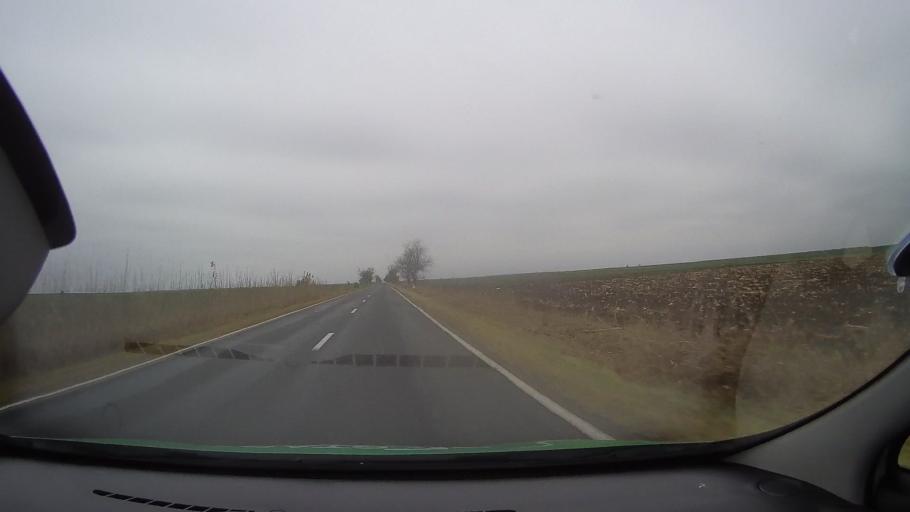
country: RO
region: Braila
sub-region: Comuna Baraganul
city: Baraganul
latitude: 44.7784
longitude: 27.4817
